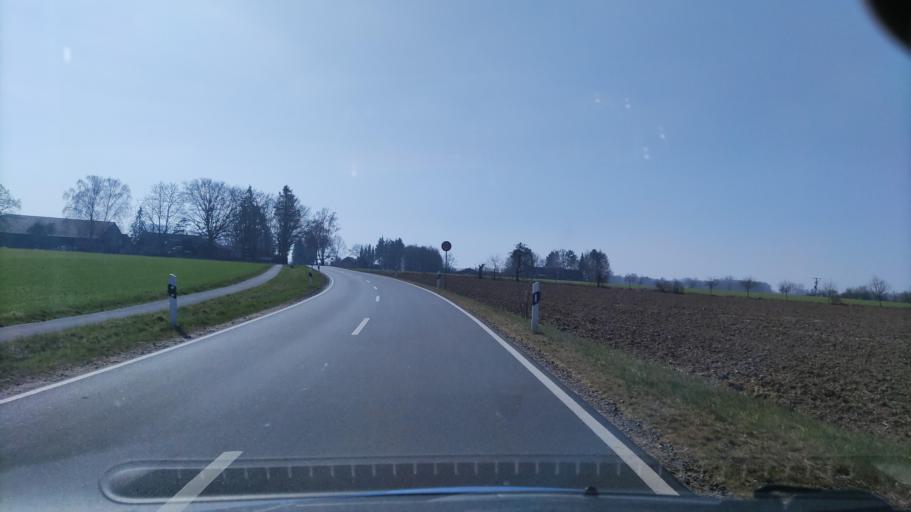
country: DE
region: Lower Saxony
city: Waddeweitz
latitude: 52.9707
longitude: 10.9707
